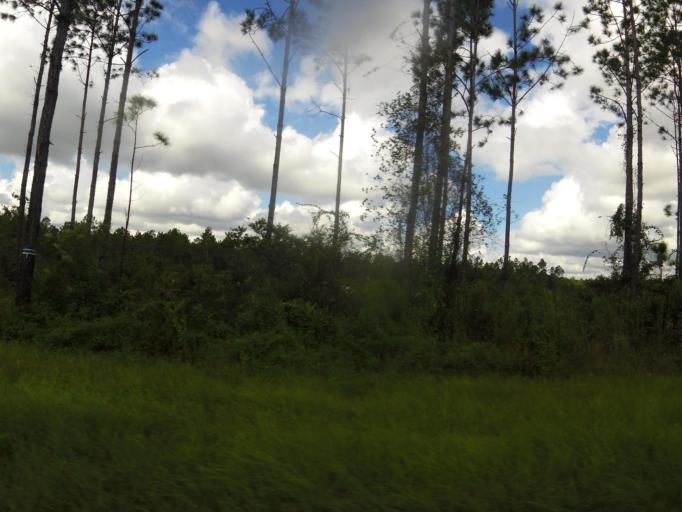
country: US
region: Florida
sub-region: Saint Johns County
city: Palm Valley
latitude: 30.0487
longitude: -81.4007
